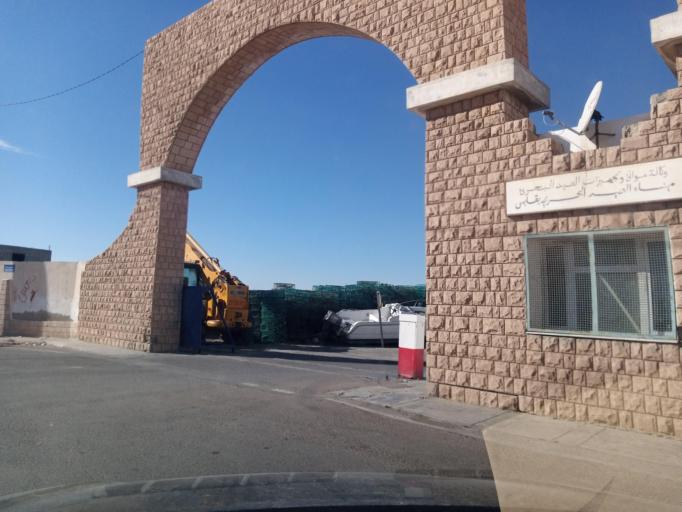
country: TN
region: Qabis
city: Gabes
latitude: 33.8944
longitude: 10.1140
